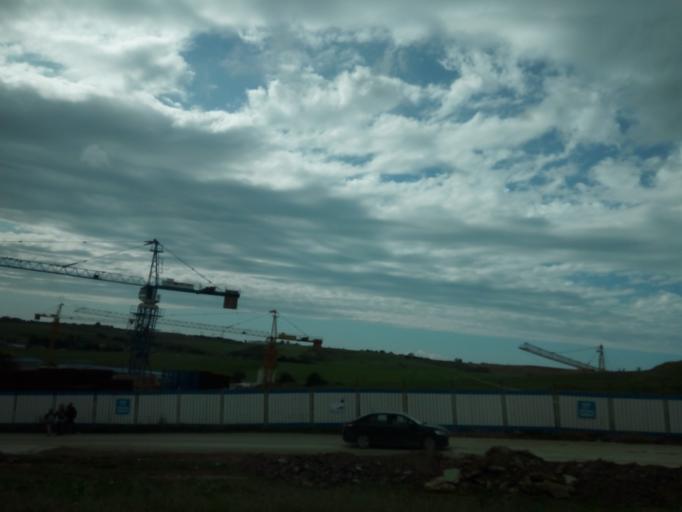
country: DZ
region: Tipaza
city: Douera
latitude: 36.6943
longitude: 2.9613
